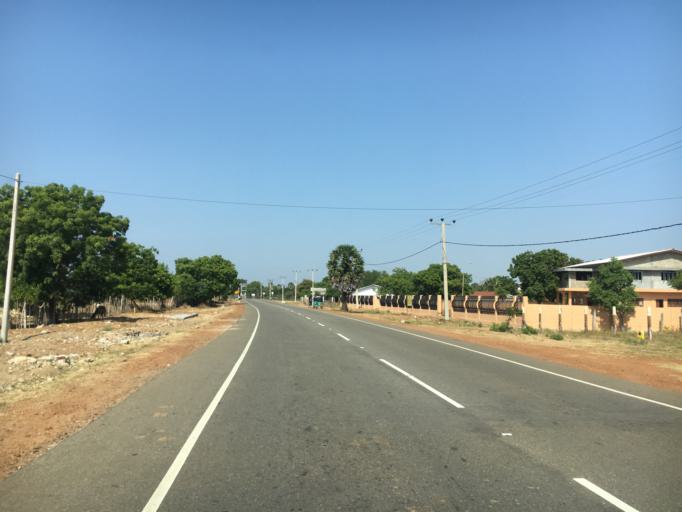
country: LK
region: Northern Province
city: Kilinochchi
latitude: 9.4375
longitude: 80.4048
